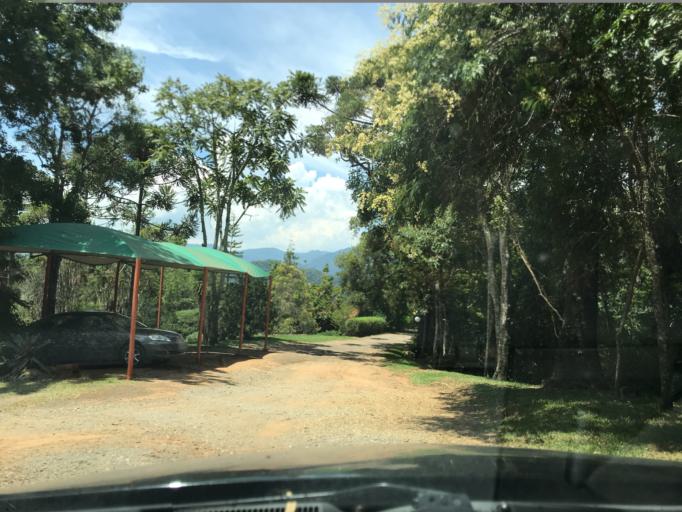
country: BR
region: Sao Paulo
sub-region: Campos Do Jordao
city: Campos do Jordao
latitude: -22.8337
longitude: -45.6694
